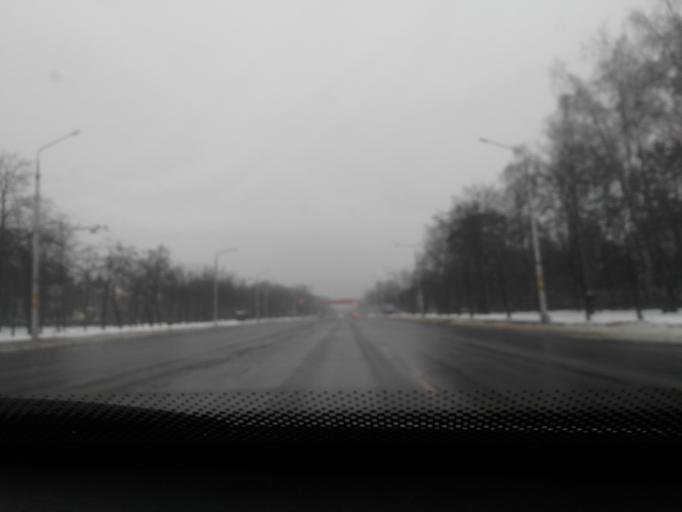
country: BY
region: Mogilev
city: Babruysk
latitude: 53.1692
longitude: 29.2059
